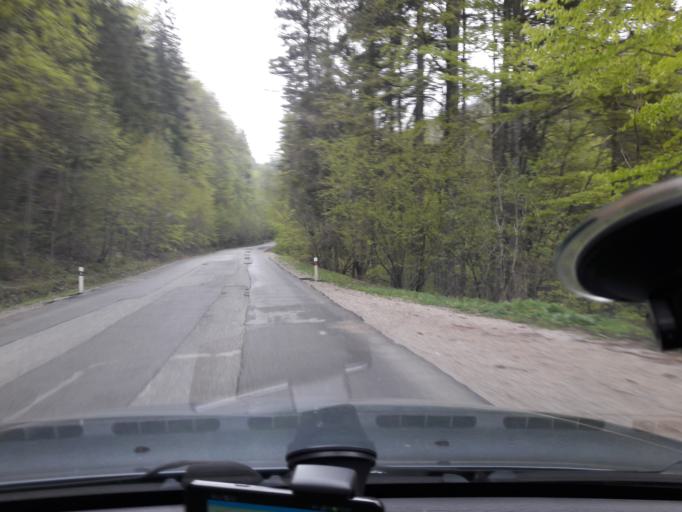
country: SK
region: Banskobystricky
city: Revuca
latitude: 48.7824
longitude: 20.1212
